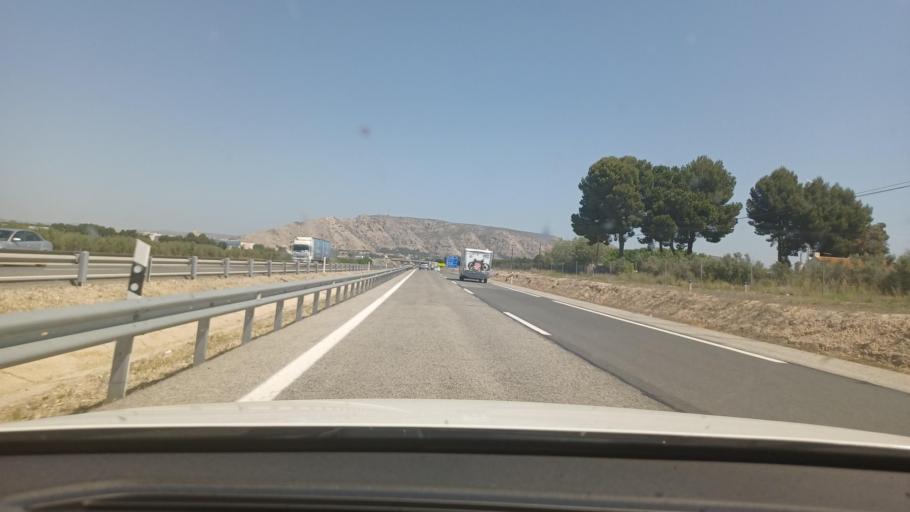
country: ES
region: Valencia
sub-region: Provincia de Alicante
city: Villena
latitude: 38.6020
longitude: -0.8450
